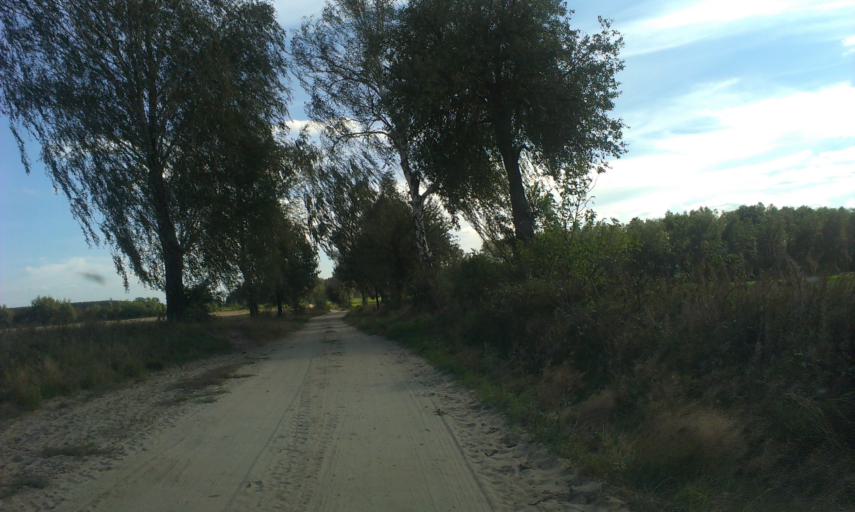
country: PL
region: Greater Poland Voivodeship
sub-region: Powiat pilski
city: Lobzenica
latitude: 53.2902
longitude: 17.1604
